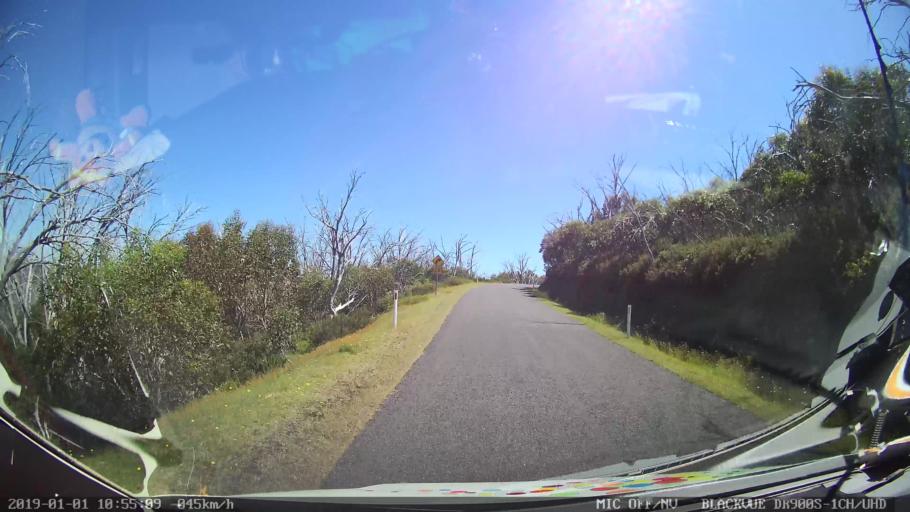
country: AU
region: New South Wales
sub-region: Snowy River
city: Jindabyne
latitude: -36.0095
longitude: 148.3875
